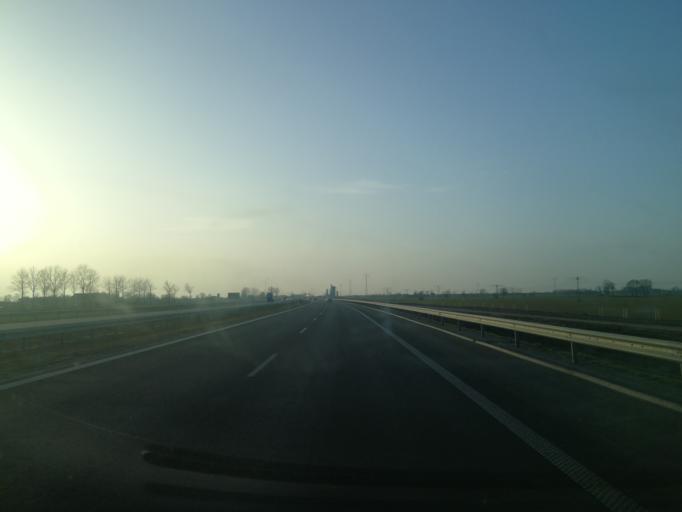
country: PL
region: Pomeranian Voivodeship
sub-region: Powiat nowodworski
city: Ostaszewo
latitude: 54.2532
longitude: 18.9749
